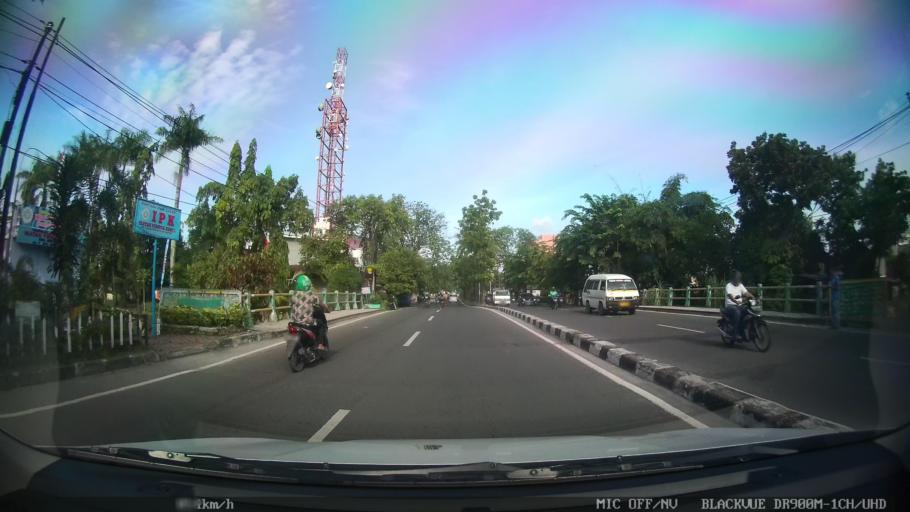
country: ID
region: North Sumatra
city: Medan
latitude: 3.6072
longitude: 98.6610
